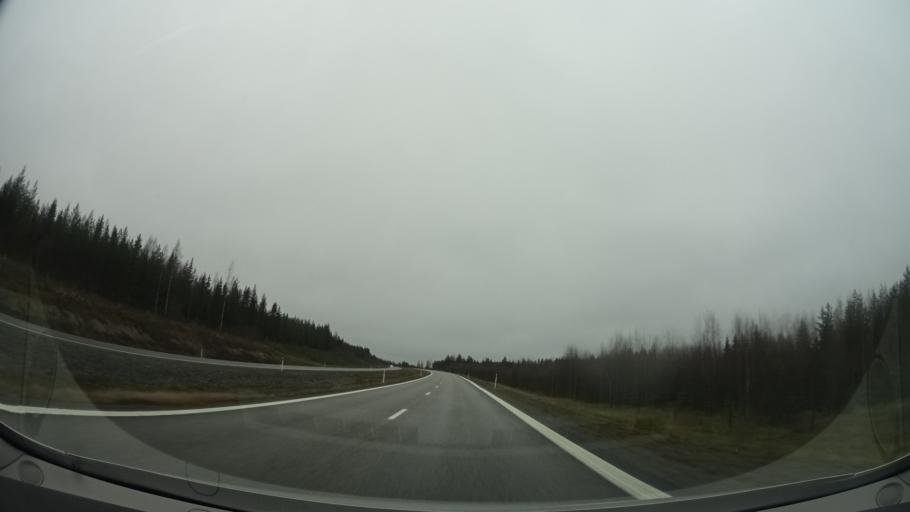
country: SE
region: Vaesterbotten
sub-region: Skelleftea Kommun
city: Kage
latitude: 64.8104
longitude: 21.0327
